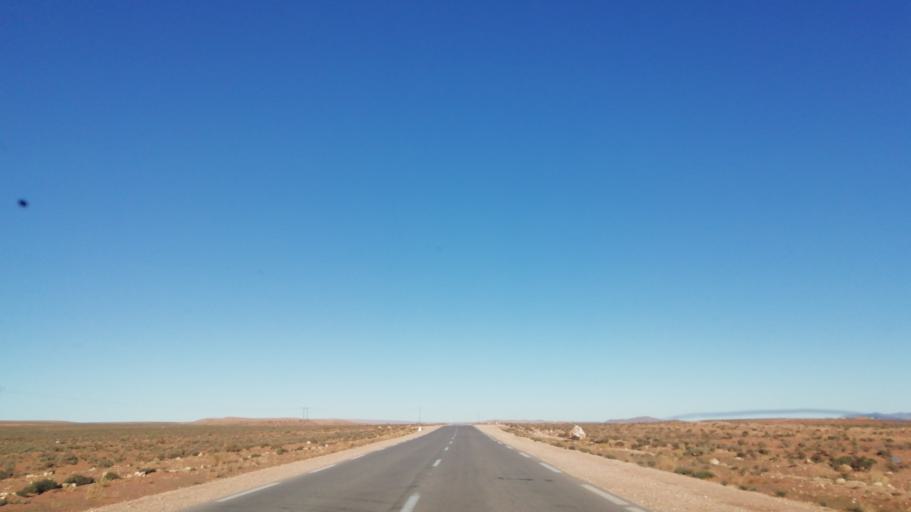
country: DZ
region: El Bayadh
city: El Abiodh Sidi Cheikh
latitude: 33.1265
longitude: 0.2828
